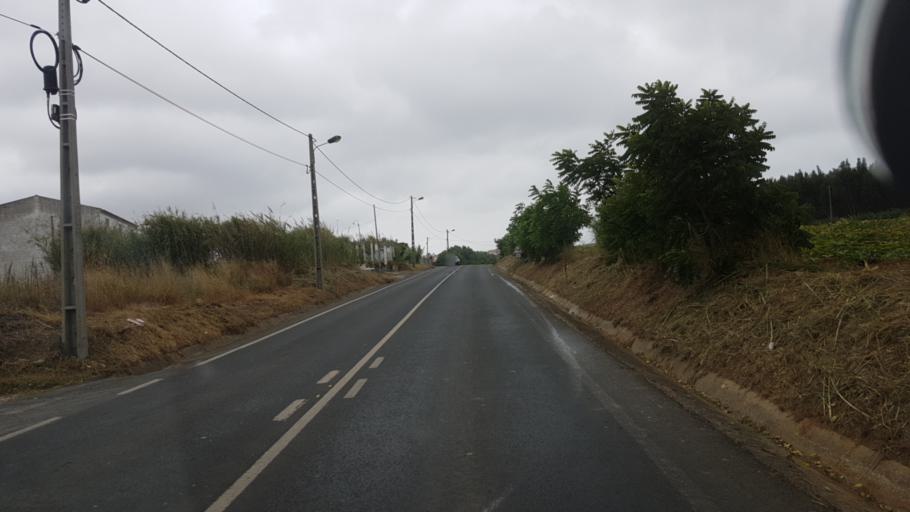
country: PT
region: Lisbon
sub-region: Lourinha
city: Lourinha
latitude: 39.2277
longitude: -9.3122
